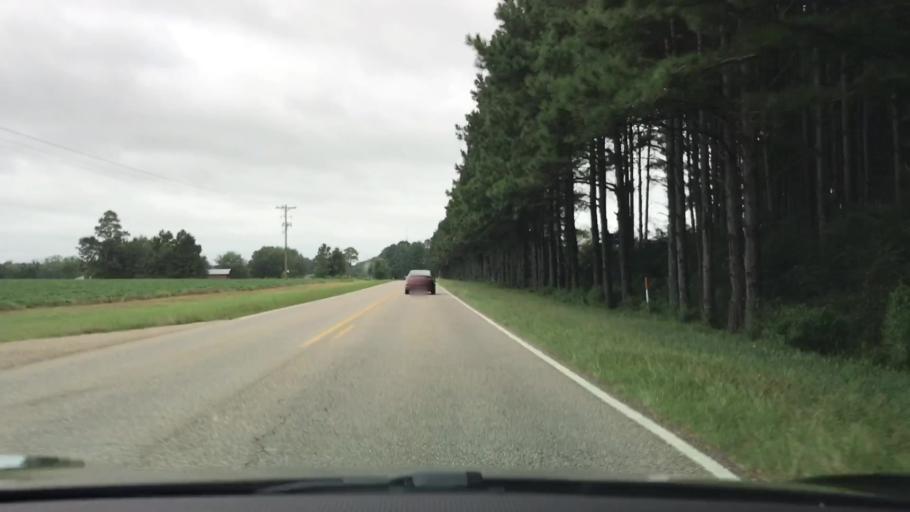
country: US
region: Alabama
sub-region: Geneva County
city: Samson
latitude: 31.1580
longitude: -86.1416
